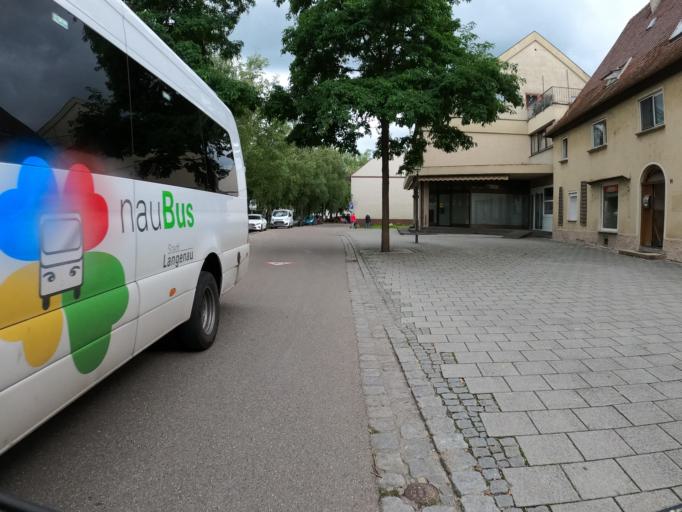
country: DE
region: Baden-Wuerttemberg
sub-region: Tuebingen Region
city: Langenau
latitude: 48.4983
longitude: 10.1193
